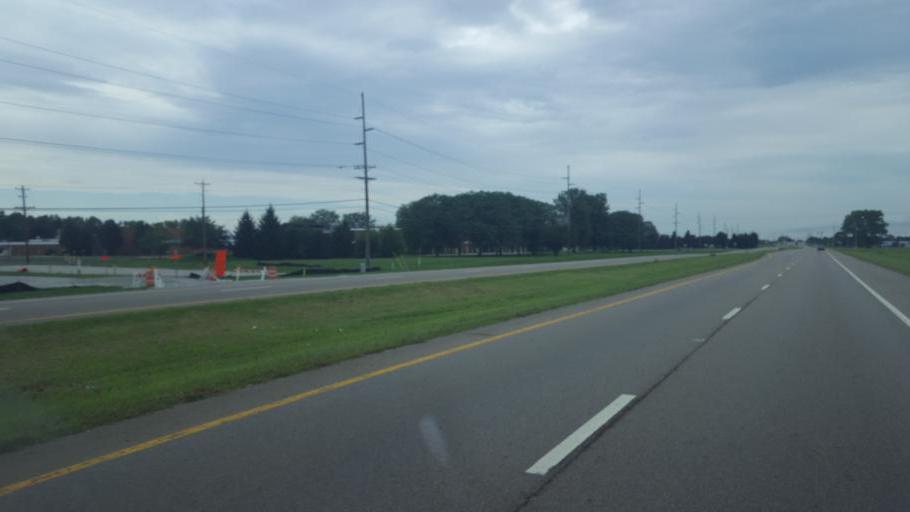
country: US
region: Ohio
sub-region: Franklin County
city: Groveport
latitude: 39.8804
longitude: -82.8837
